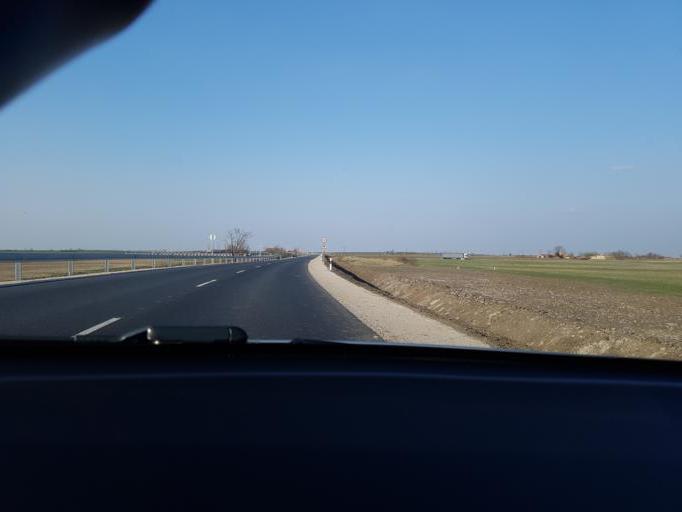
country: RO
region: Arad
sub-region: Comuna Nadlac
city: Nadlac
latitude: 46.1941
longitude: 20.7135
